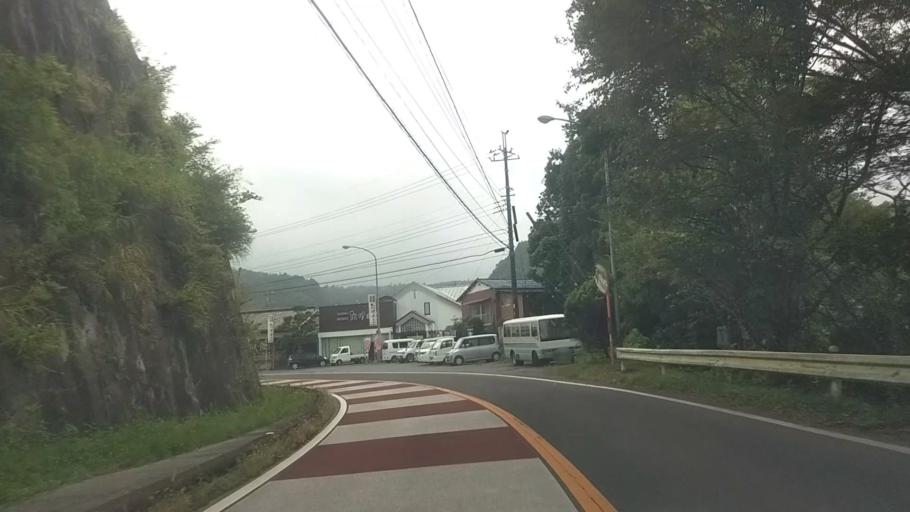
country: JP
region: Chiba
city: Katsuura
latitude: 35.2419
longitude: 140.2380
